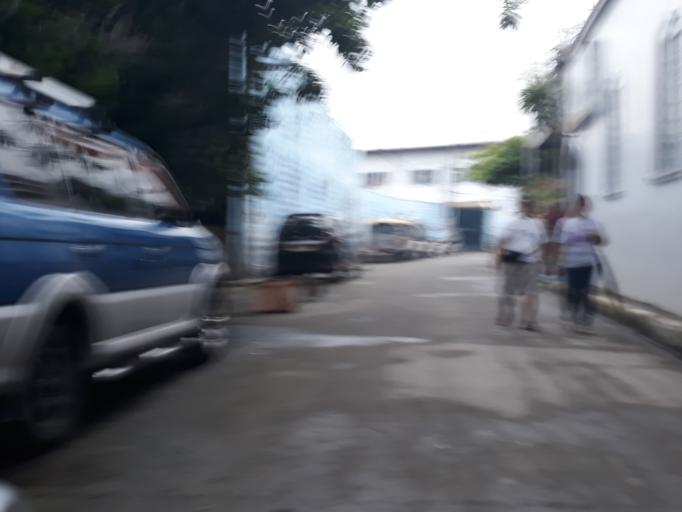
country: PH
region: Metro Manila
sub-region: San Juan
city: San Juan
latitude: 14.6117
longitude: 121.0234
